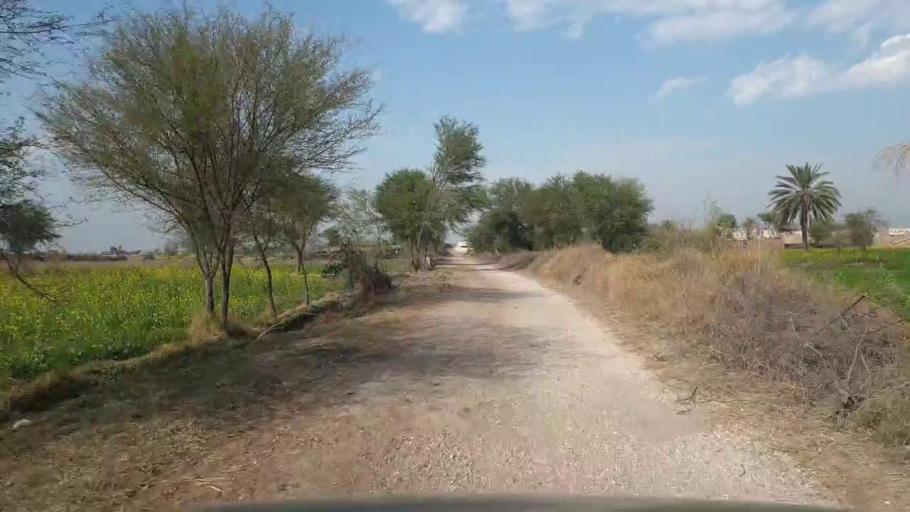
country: PK
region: Sindh
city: Sakrand
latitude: 26.0202
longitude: 68.4171
